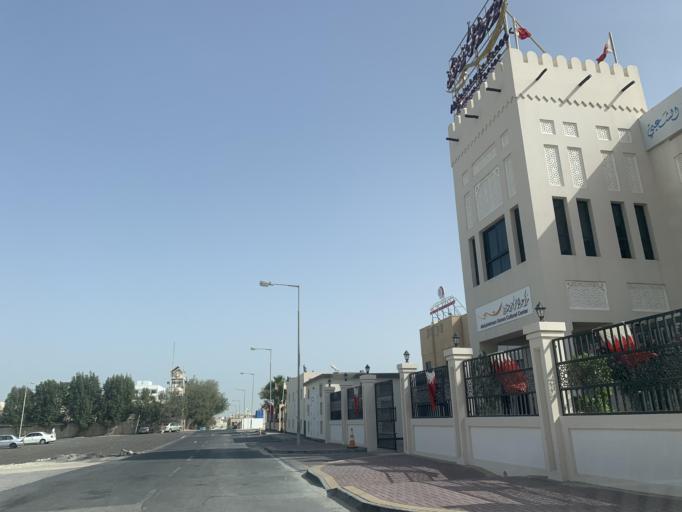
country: BH
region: Northern
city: Ar Rifa'
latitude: 26.1525
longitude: 50.5680
